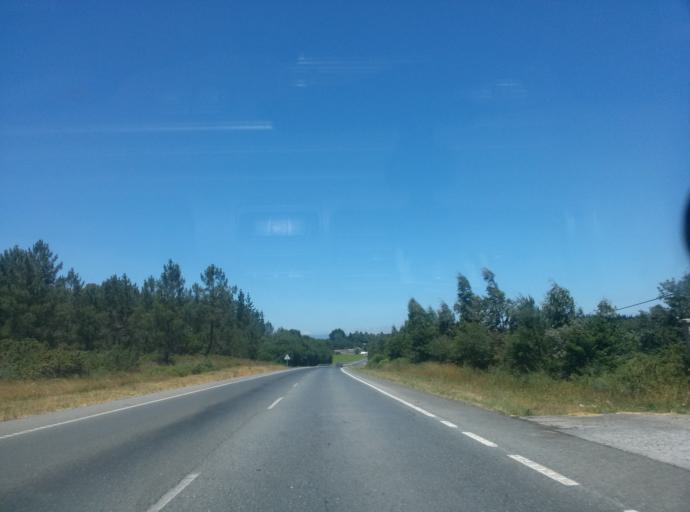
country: ES
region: Galicia
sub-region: Provincia de Lugo
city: Mos
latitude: 43.1161
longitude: -7.4850
